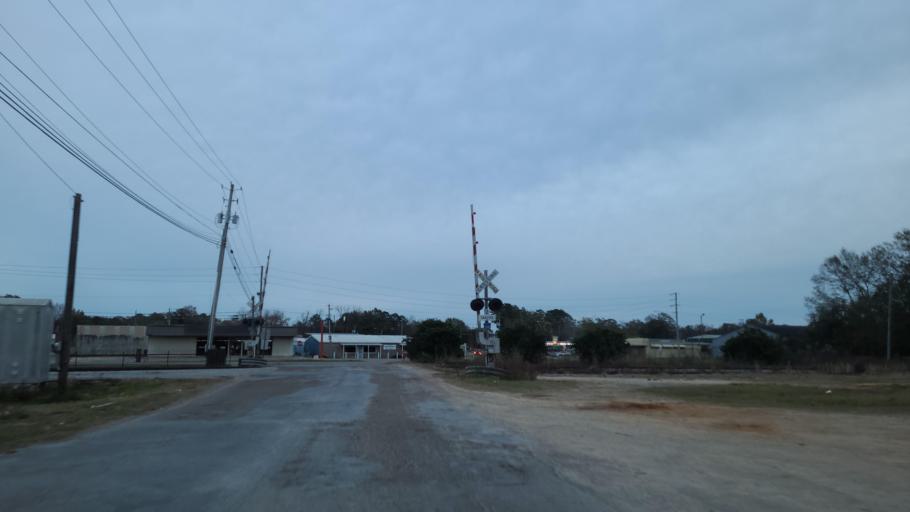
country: US
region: Mississippi
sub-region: Clarke County
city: Quitman
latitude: 32.0392
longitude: -88.7310
